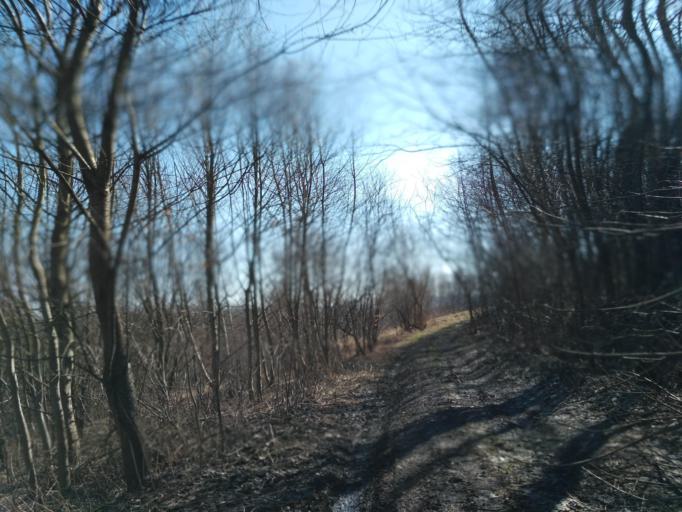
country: PL
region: Subcarpathian Voivodeship
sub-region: Powiat brzozowski
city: Domaradz
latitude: 49.7997
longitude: 21.9660
